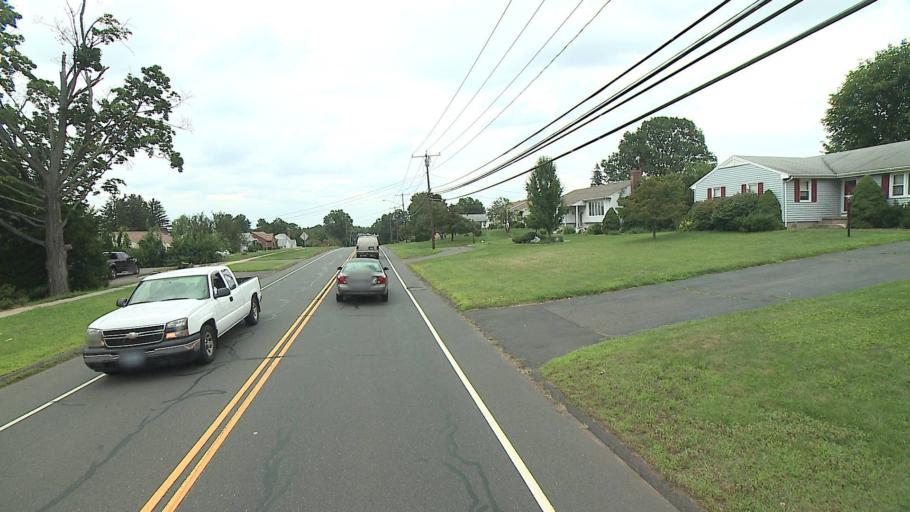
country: US
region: Connecticut
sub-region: Hartford County
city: Wethersfield
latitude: 41.6768
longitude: -72.6660
